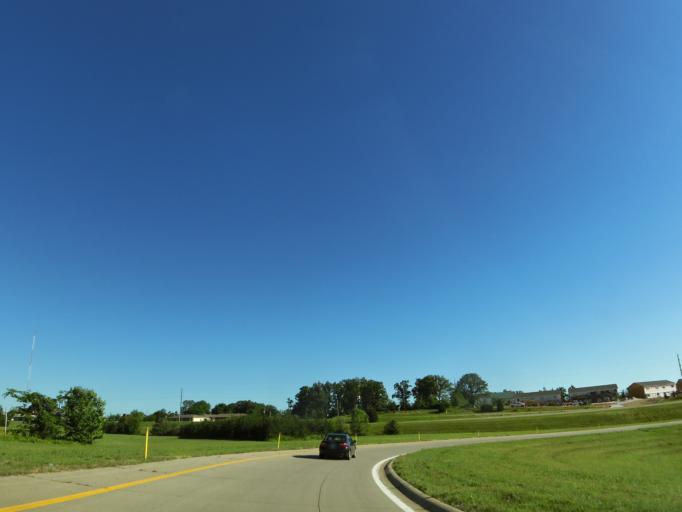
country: US
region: Missouri
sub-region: Butler County
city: Poplar Bluff
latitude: 36.7957
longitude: -90.4442
